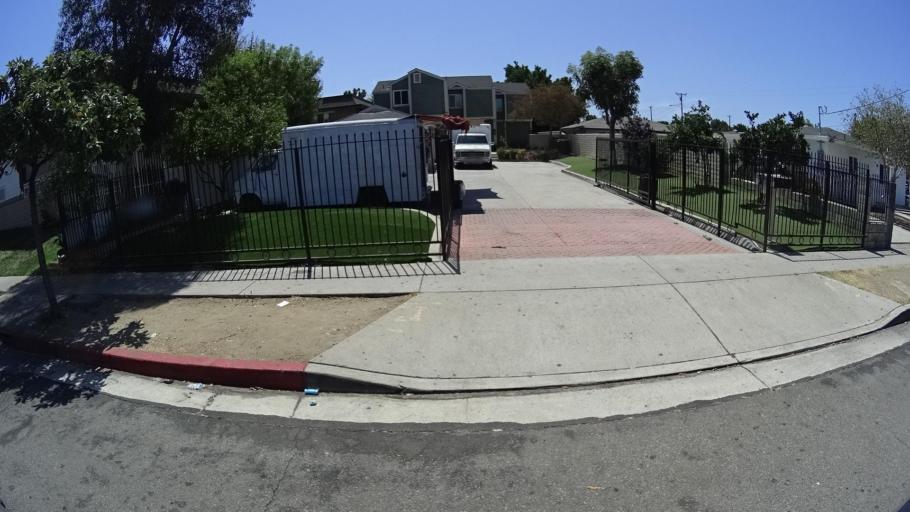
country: US
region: California
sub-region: Orange County
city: Placentia
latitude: 33.8563
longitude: -117.8820
